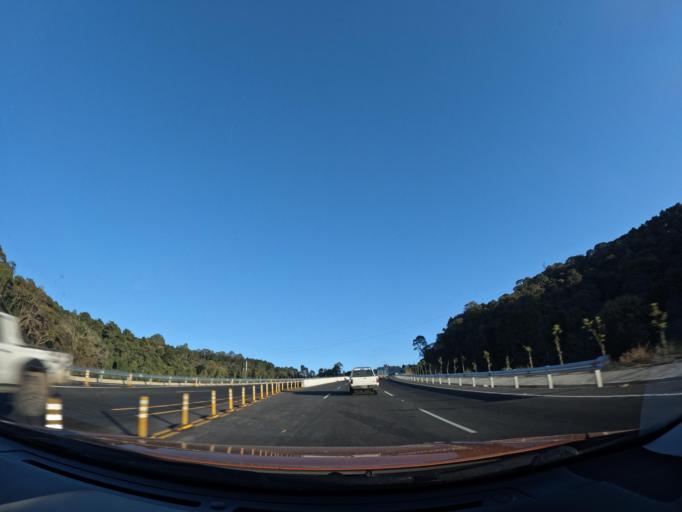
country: GT
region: Guatemala
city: Villa Canales
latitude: 14.4860
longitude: -90.4914
